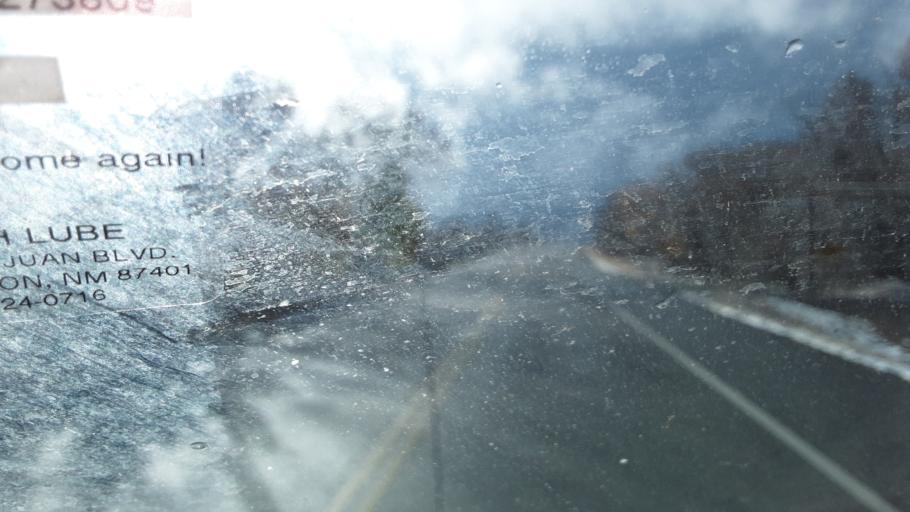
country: US
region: Colorado
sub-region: La Plata County
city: Bayfield
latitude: 37.2182
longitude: -107.6408
